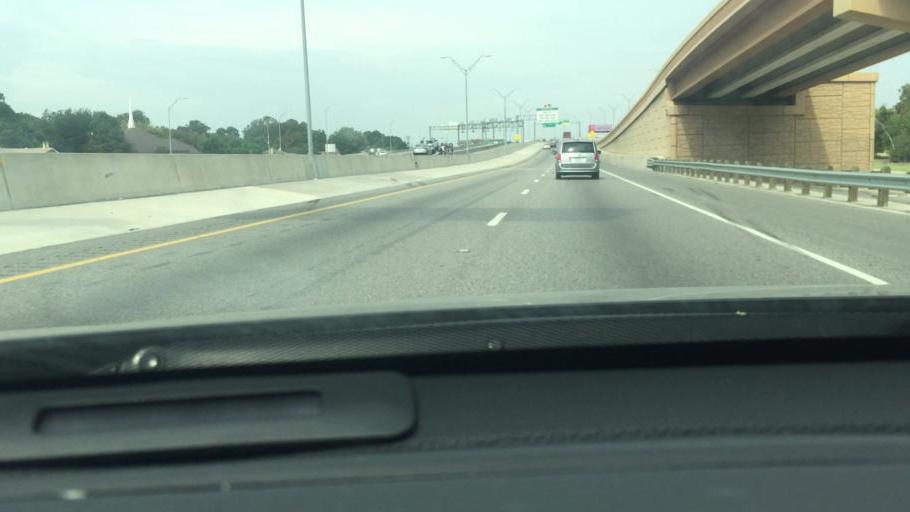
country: US
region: Texas
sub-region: Tarrant County
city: North Richland Hills
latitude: 32.8361
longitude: -97.2226
